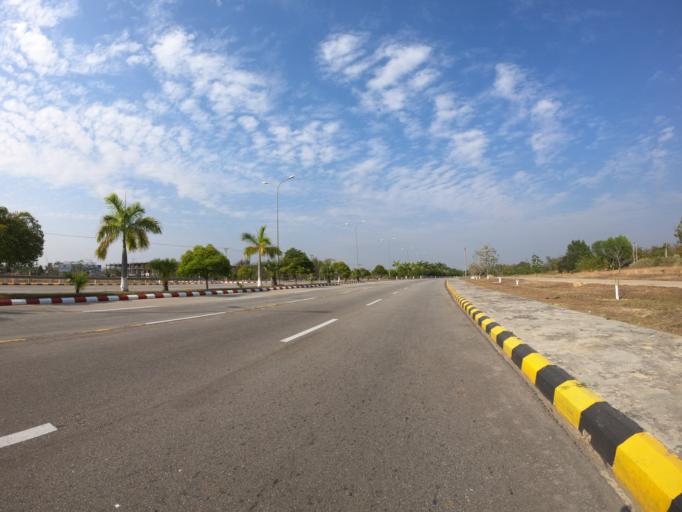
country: MM
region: Mandalay
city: Nay Pyi Taw
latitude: 19.6888
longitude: 96.1259
